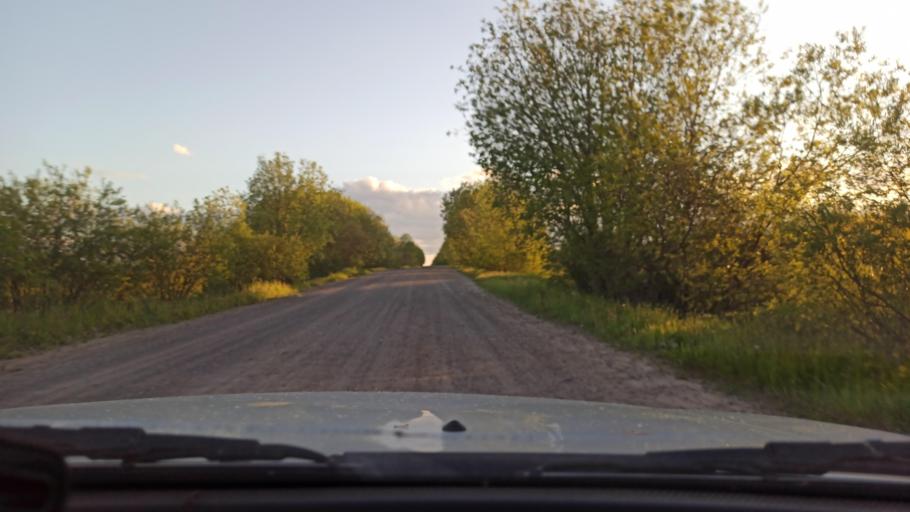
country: RU
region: Vologda
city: Molochnoye
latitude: 59.3713
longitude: 39.6938
